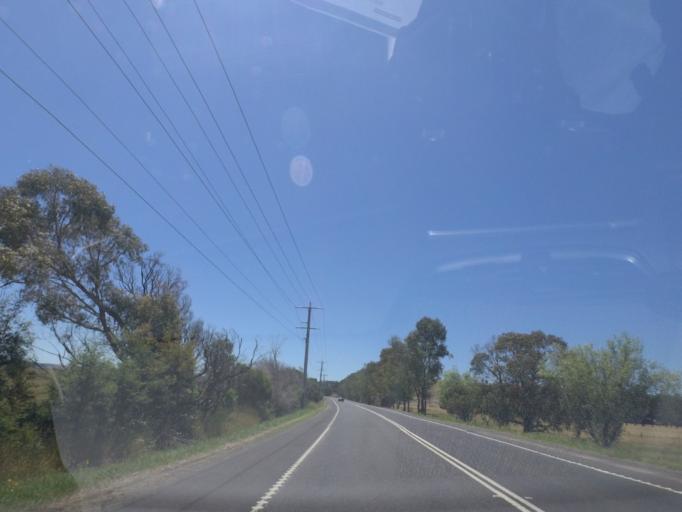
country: AU
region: Victoria
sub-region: Whittlesea
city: Whittlesea
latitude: -37.4548
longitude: 145.0318
